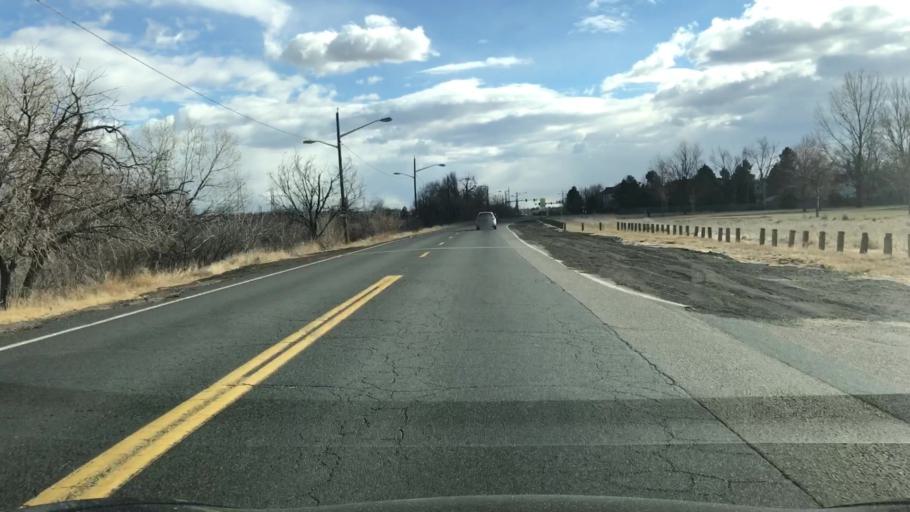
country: US
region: Colorado
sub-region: Arapahoe County
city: Glendale
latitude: 39.6871
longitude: -104.9071
